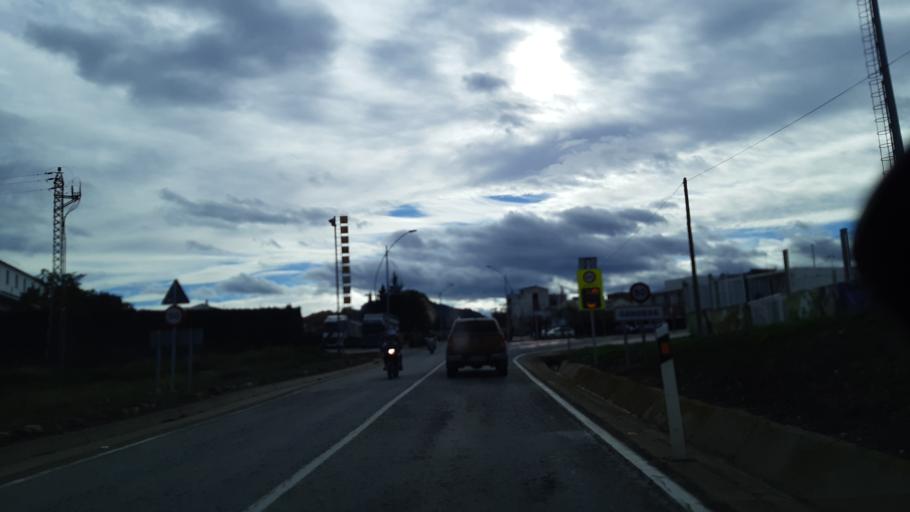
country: ES
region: Catalonia
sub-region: Provincia de Tarragona
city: Gandesa
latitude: 41.0589
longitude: 0.4416
